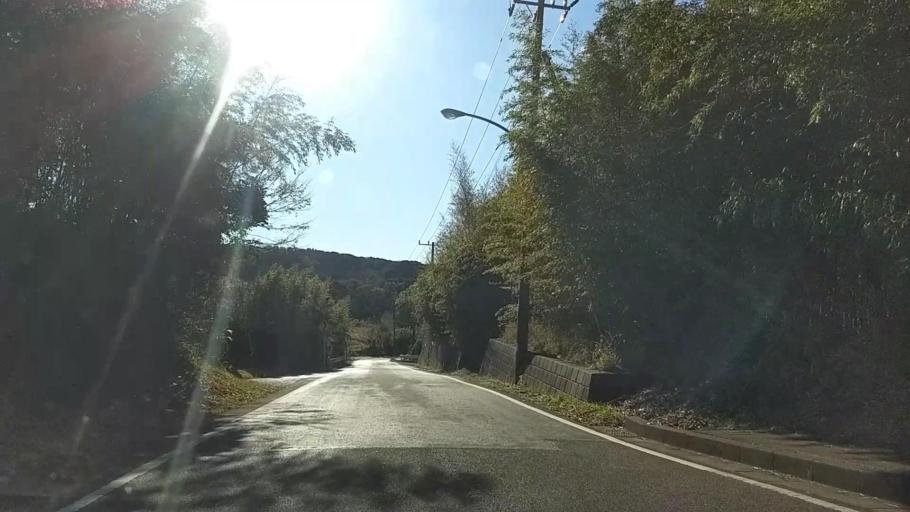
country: JP
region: Chiba
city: Futtsu
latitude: 35.2333
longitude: 139.8765
